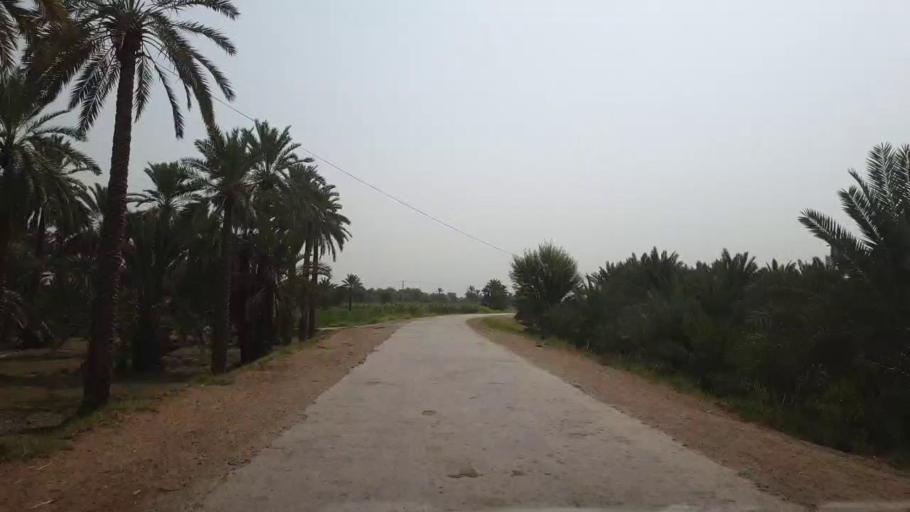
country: PK
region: Sindh
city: Gambat
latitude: 27.4314
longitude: 68.5273
